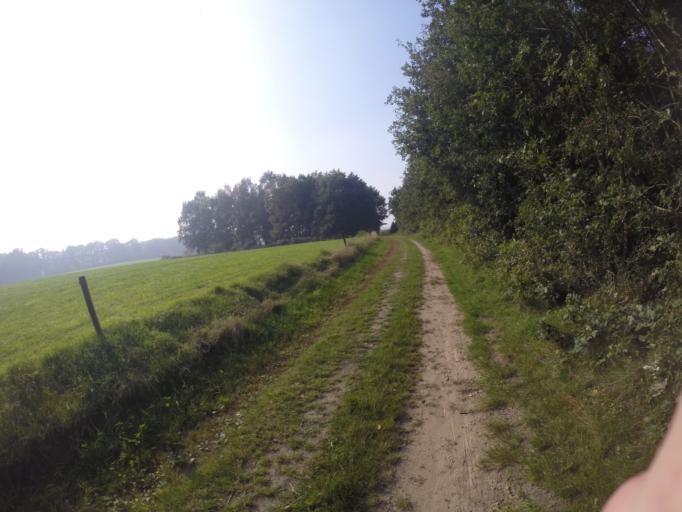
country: NL
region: Gelderland
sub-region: Gemeente Lochem
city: Laren
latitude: 52.1591
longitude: 6.3470
